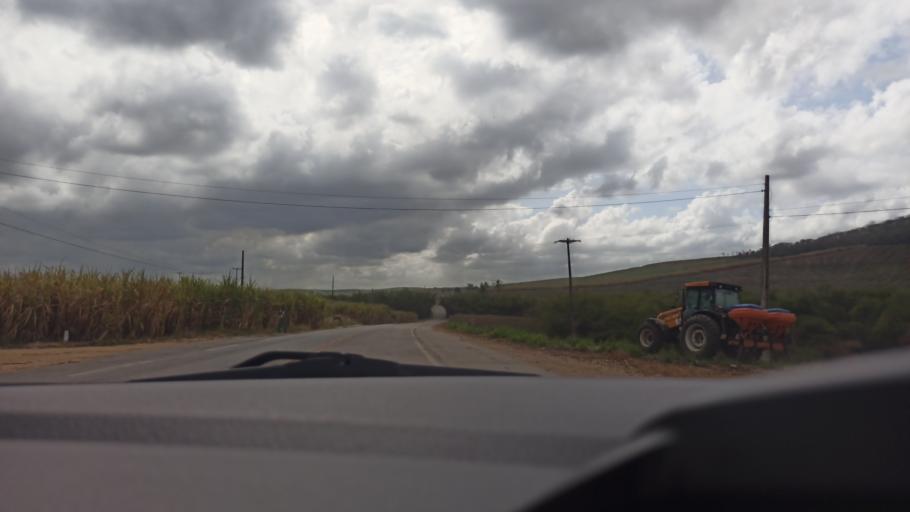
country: BR
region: Pernambuco
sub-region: Timbauba
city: Timbauba
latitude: -7.5456
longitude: -35.2673
